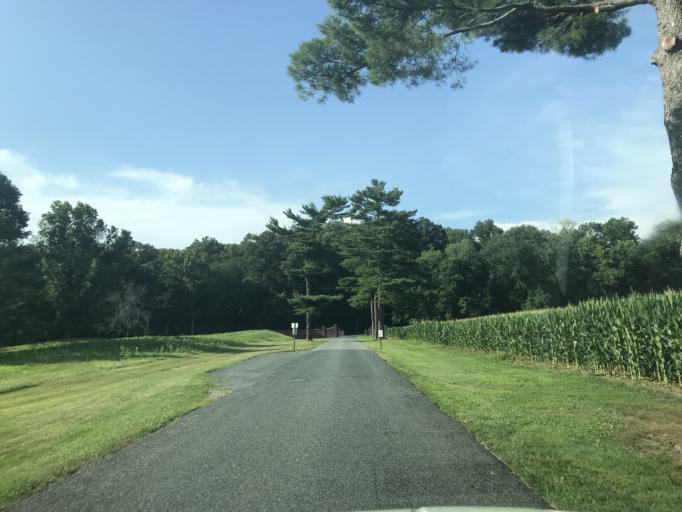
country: US
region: Maryland
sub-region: Harford County
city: Aberdeen
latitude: 39.5116
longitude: -76.1256
